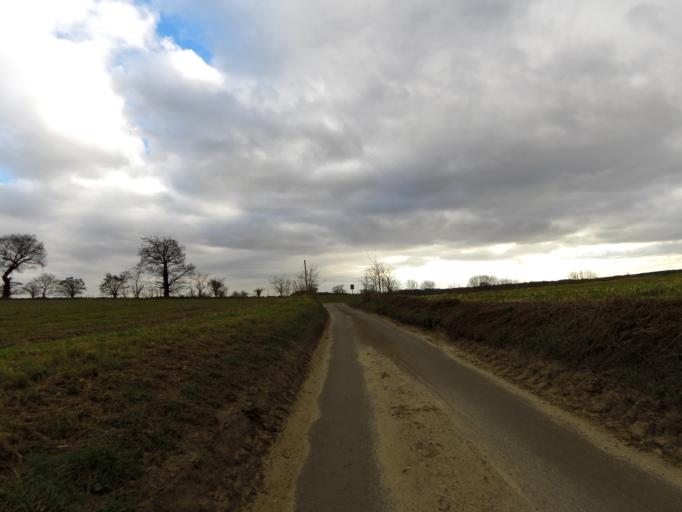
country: GB
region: England
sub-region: Suffolk
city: Woodbridge
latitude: 52.0412
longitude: 1.3214
